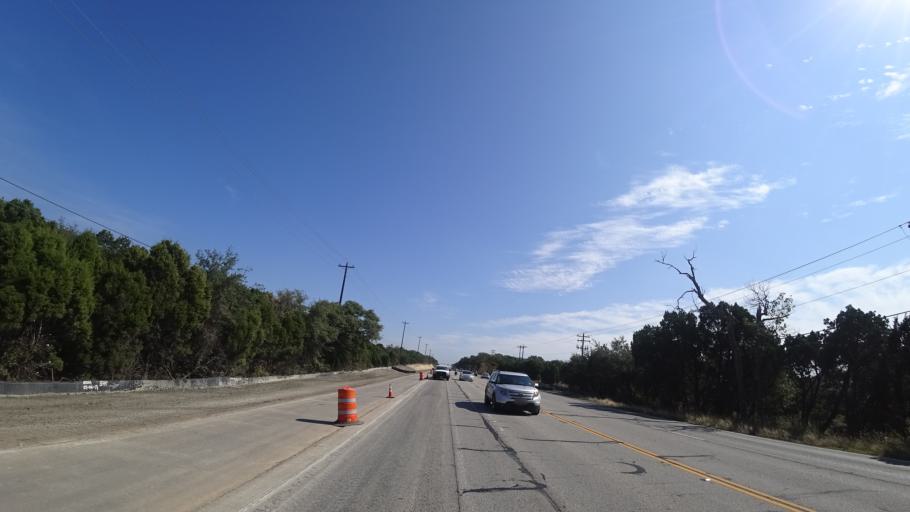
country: US
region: Texas
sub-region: Travis County
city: Barton Creek
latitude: 30.2337
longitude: -97.9064
